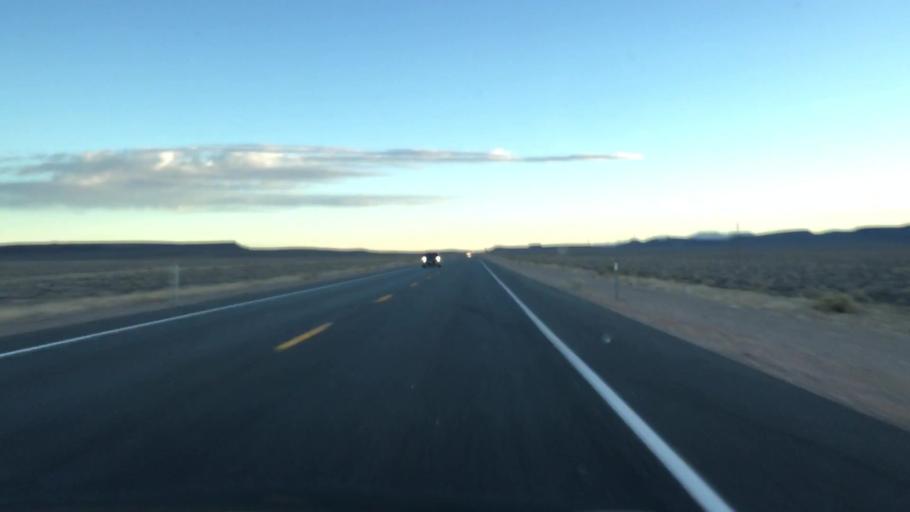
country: US
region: Nevada
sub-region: Esmeralda County
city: Goldfield
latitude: 37.4471
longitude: -117.1671
